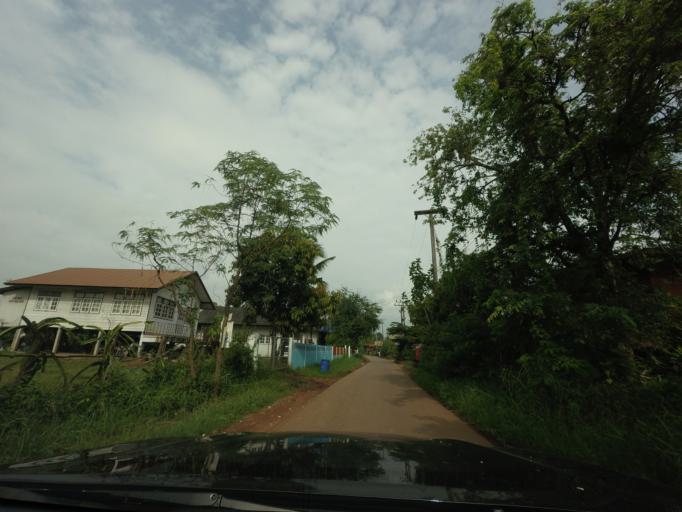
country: TH
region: Nong Khai
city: Nong Khai
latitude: 17.8144
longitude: 102.7239
